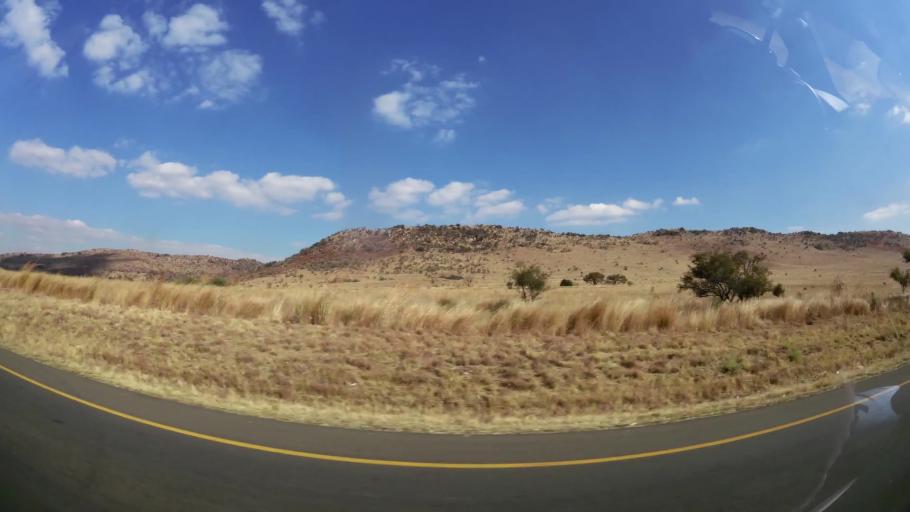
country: ZA
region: Gauteng
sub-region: West Rand District Municipality
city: Krugersdorp
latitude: -26.0373
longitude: 27.7672
